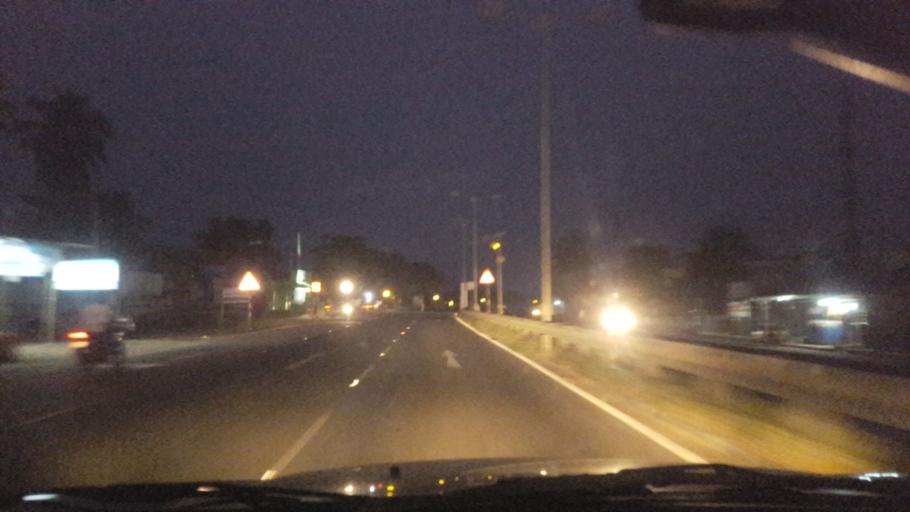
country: IN
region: Andhra Pradesh
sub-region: East Godavari
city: Peddapuram
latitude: 17.1369
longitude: 81.9587
